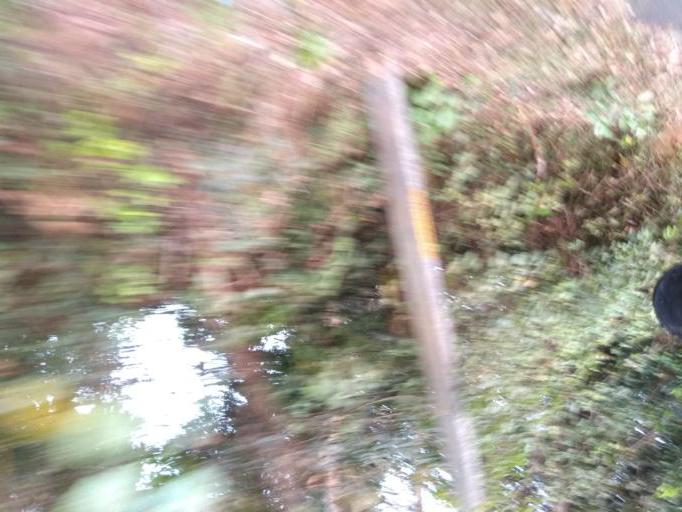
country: IN
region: Karnataka
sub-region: Dakshina Kannada
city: Mangalore
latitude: 12.9341
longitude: 74.8670
